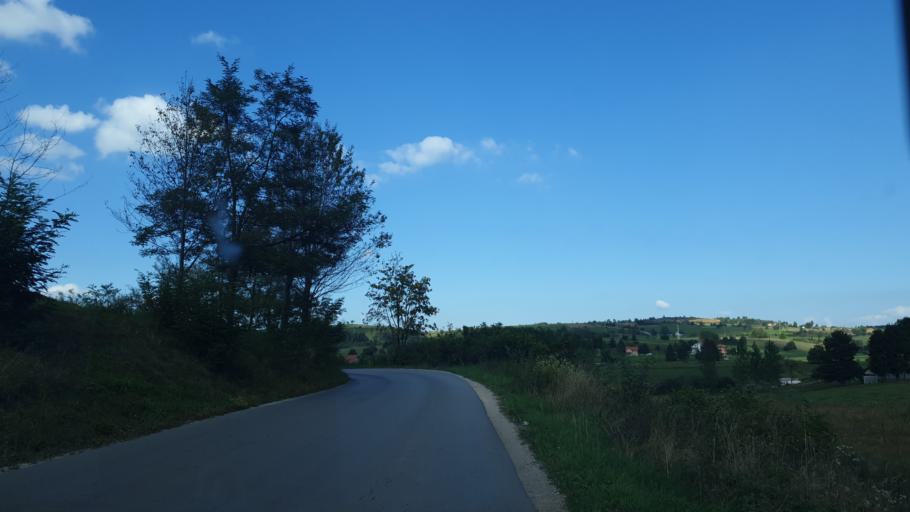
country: RS
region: Central Serbia
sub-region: Zlatiborski Okrug
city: Nova Varos
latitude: 43.4322
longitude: 19.8734
